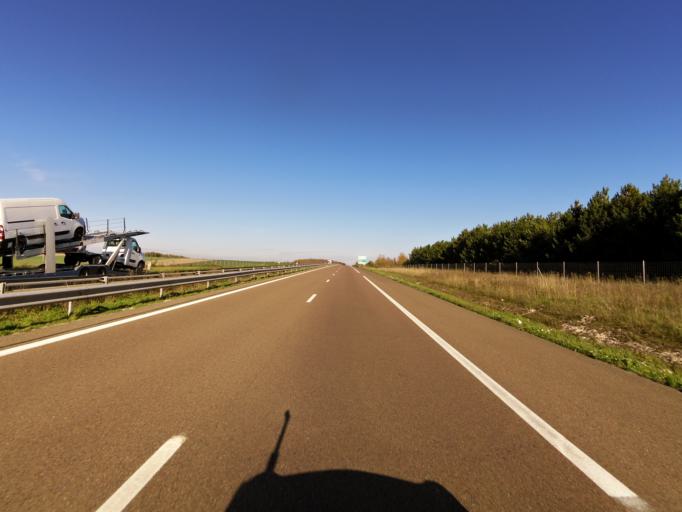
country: FR
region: Champagne-Ardenne
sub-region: Departement de la Marne
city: Compertrix
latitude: 48.8927
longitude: 4.2880
